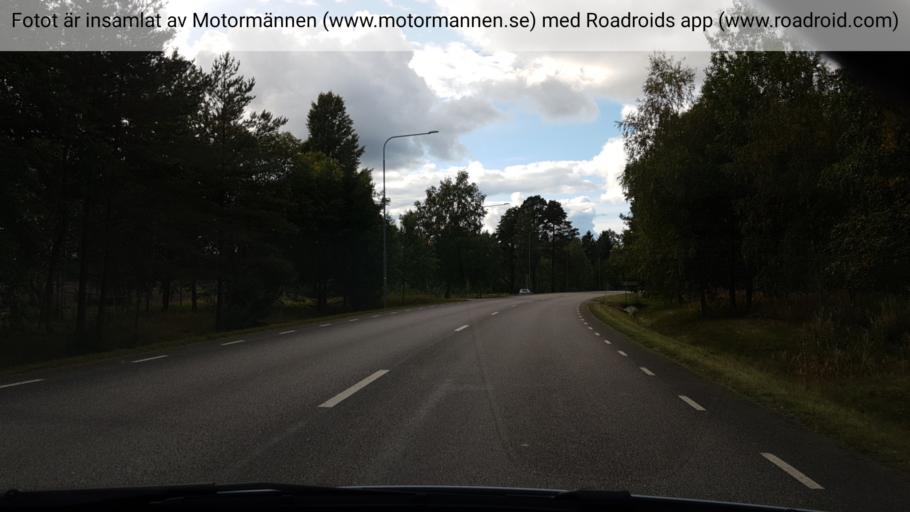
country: SE
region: Vaestra Goetaland
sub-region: Tibro Kommun
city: Tibro
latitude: 58.4105
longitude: 14.1715
